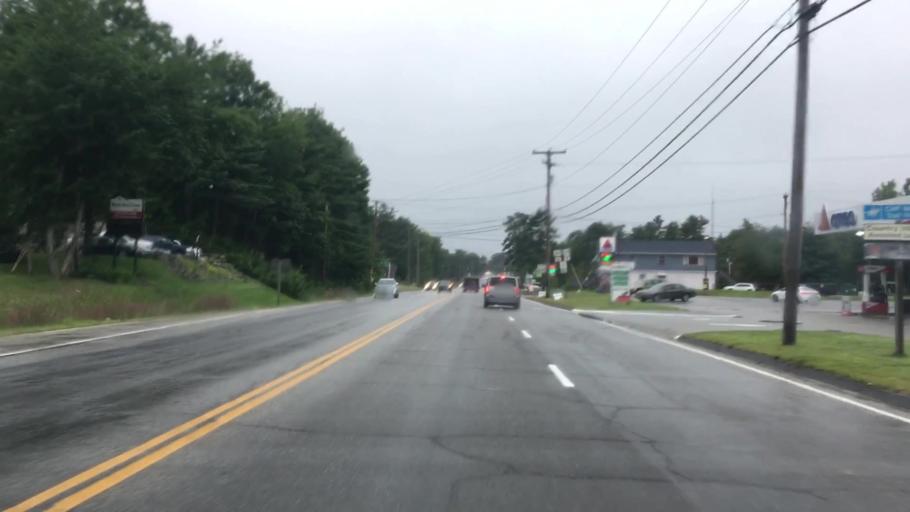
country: US
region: Maine
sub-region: Cumberland County
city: Raymond
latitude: 43.9645
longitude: -70.5764
